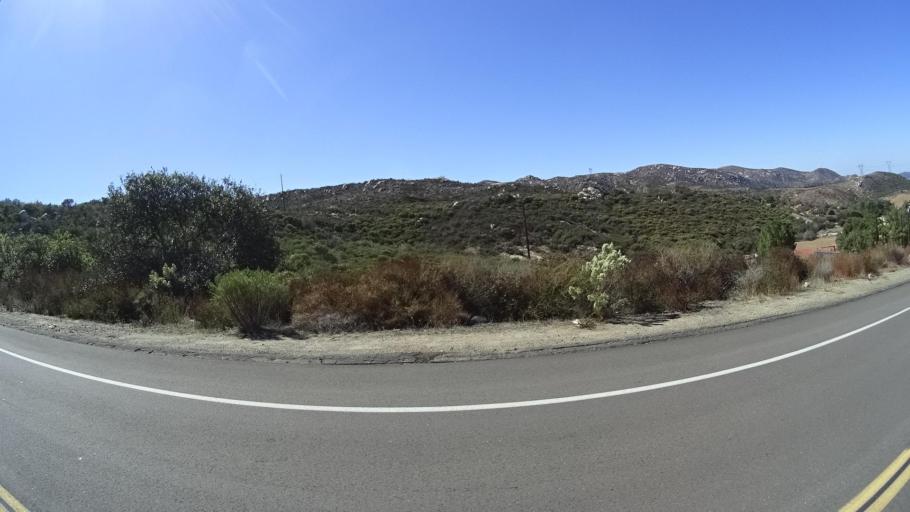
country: US
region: California
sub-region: San Diego County
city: Alpine
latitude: 32.7684
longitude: -116.6955
